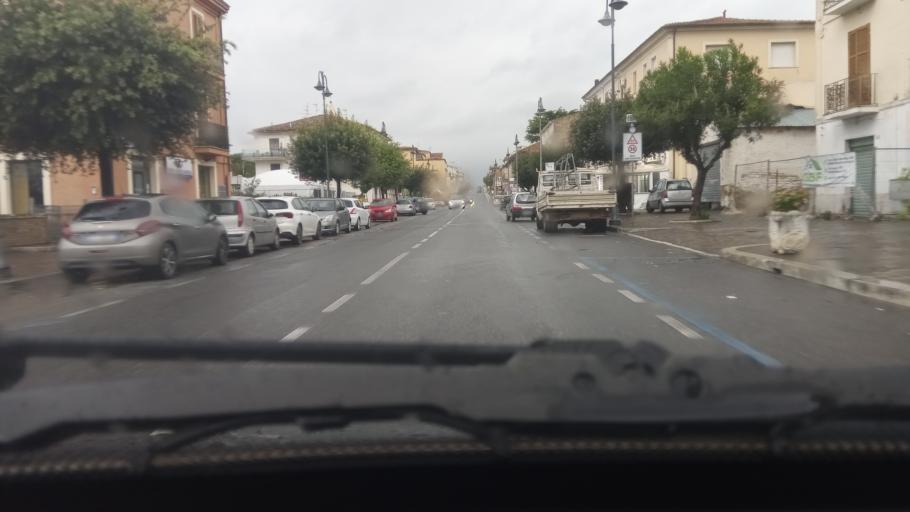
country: IT
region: Latium
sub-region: Provincia di Latina
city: Penitro
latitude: 41.2580
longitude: 13.7014
